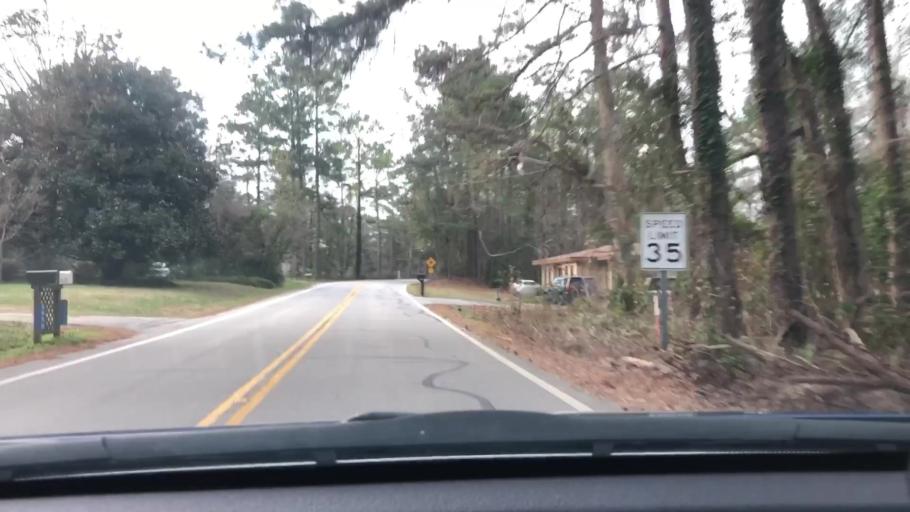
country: US
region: South Carolina
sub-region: Lexington County
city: Irmo
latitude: 34.0660
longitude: -81.1783
